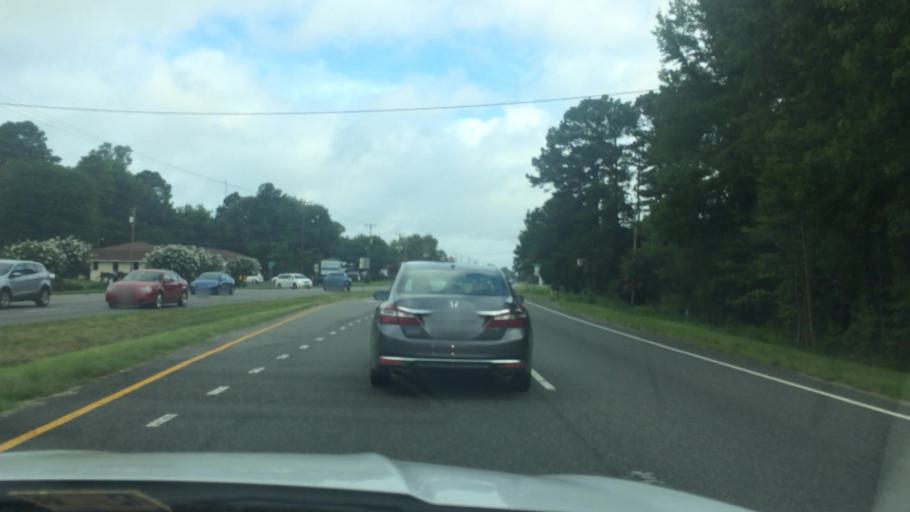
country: US
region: Virginia
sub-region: Gloucester County
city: Gloucester Point
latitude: 37.2870
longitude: -76.5080
